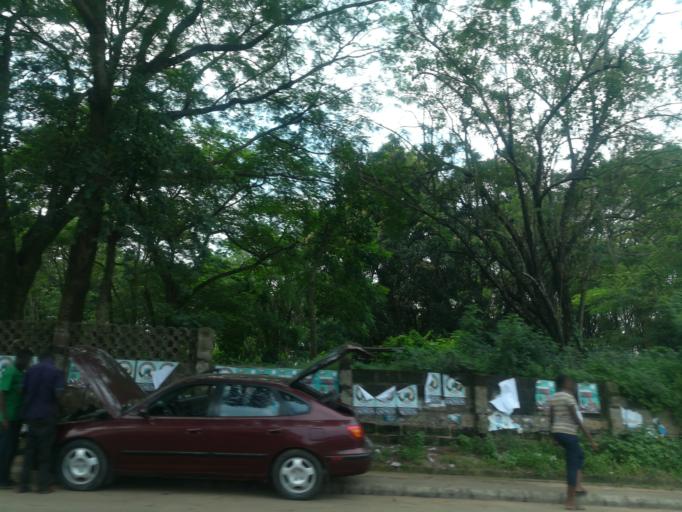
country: NG
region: Oyo
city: Ibadan
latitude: 7.4181
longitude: 3.8969
